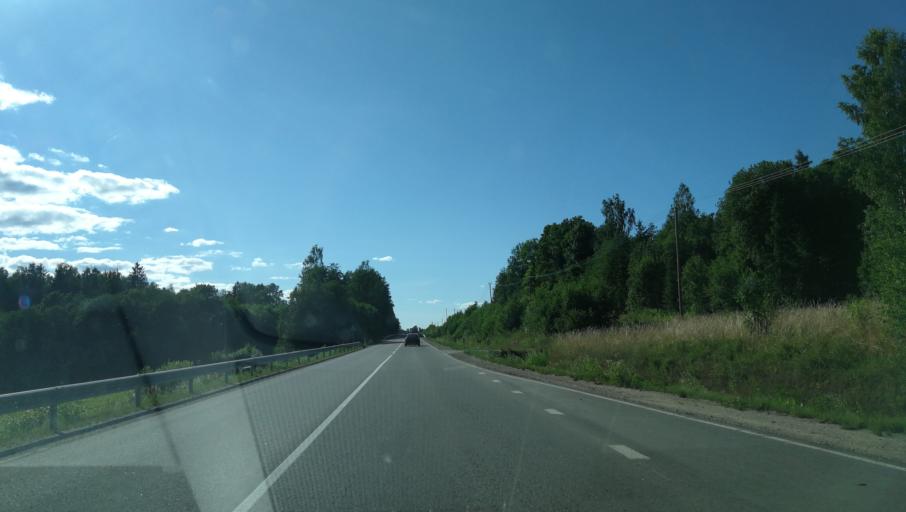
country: LV
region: Vecpiebalga
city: Vecpiebalga
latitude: 57.0716
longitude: 25.7884
